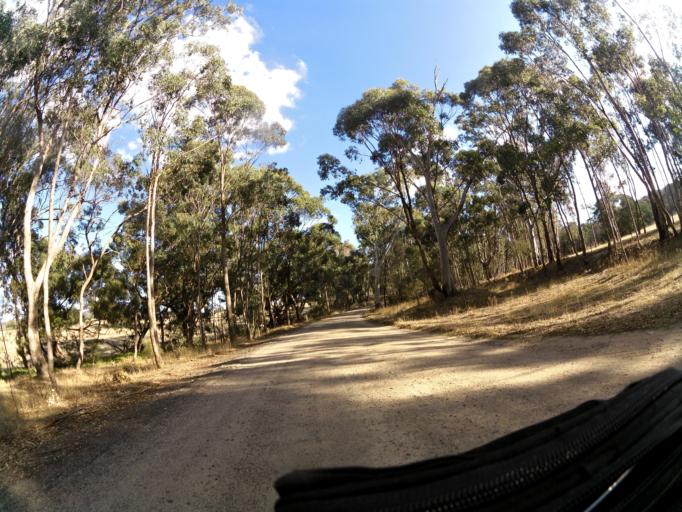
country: AU
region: Victoria
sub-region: Greater Bendigo
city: Kennington
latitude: -37.0169
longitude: 144.8074
